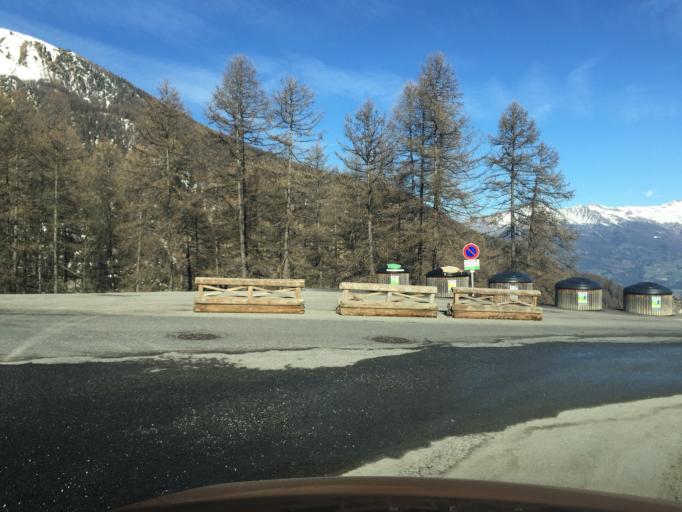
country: FR
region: Provence-Alpes-Cote d'Azur
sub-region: Departement des Hautes-Alpes
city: Embrun
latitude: 44.4828
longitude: 6.5528
